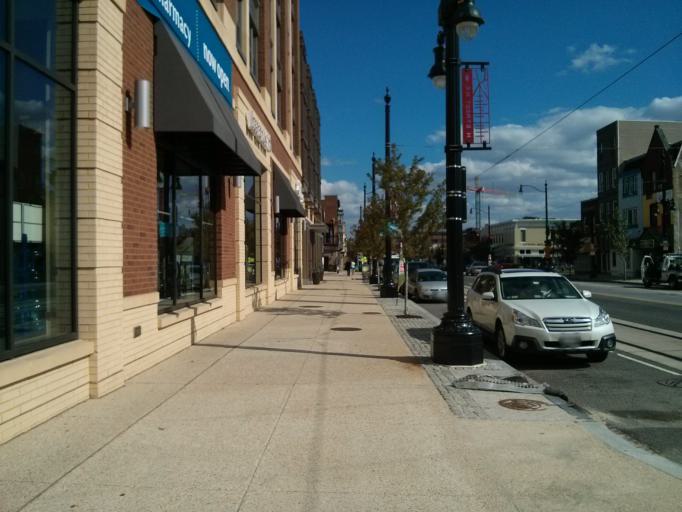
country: US
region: Washington, D.C.
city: Washington, D.C.
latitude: 38.9003
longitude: -77.0015
